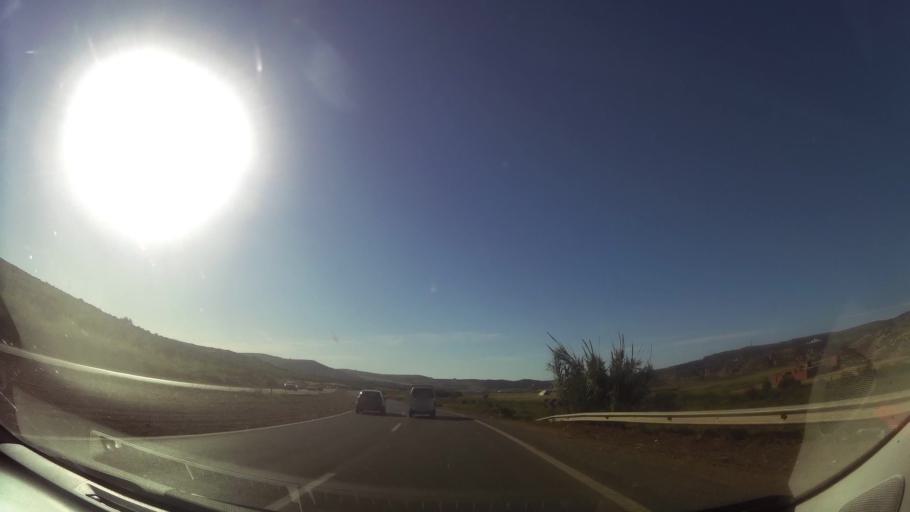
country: MA
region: Oriental
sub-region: Berkane-Taourirt
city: Ahfir
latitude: 35.0355
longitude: -2.2043
